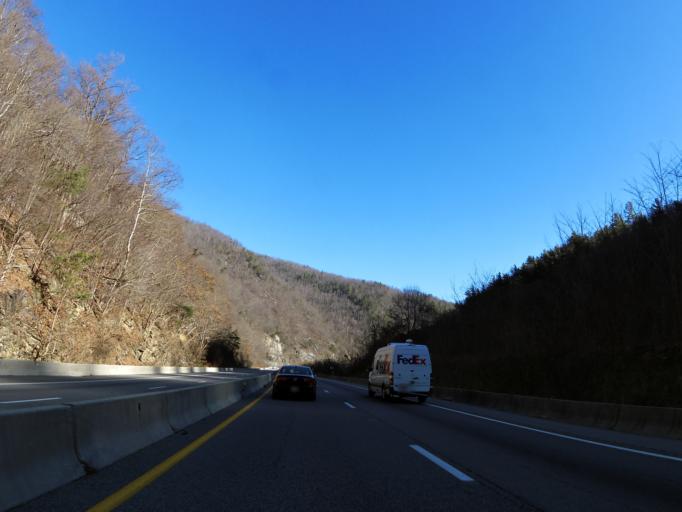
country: US
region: North Carolina
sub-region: Haywood County
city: Cove Creek
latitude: 35.7522
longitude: -83.0579
